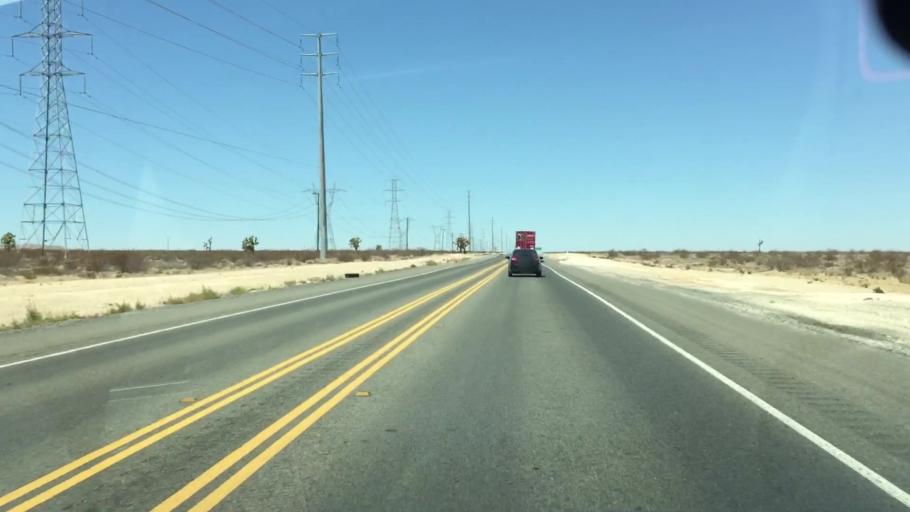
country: US
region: California
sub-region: San Bernardino County
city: Adelanto
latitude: 34.7067
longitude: -117.4556
